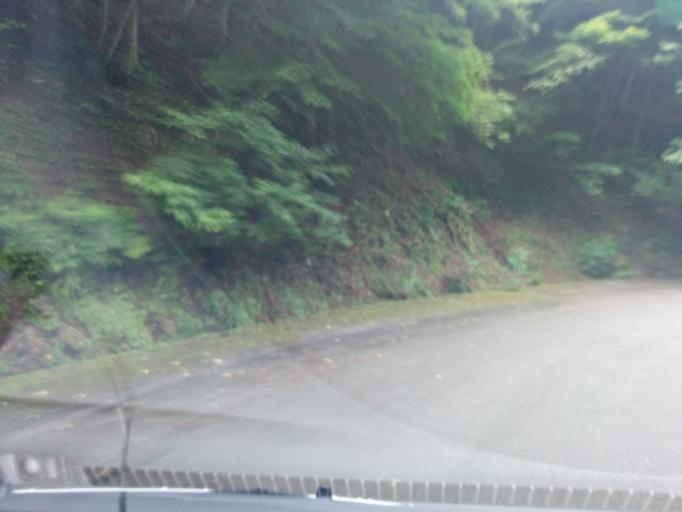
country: JP
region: Kyoto
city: Miyazu
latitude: 35.4548
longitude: 135.1144
